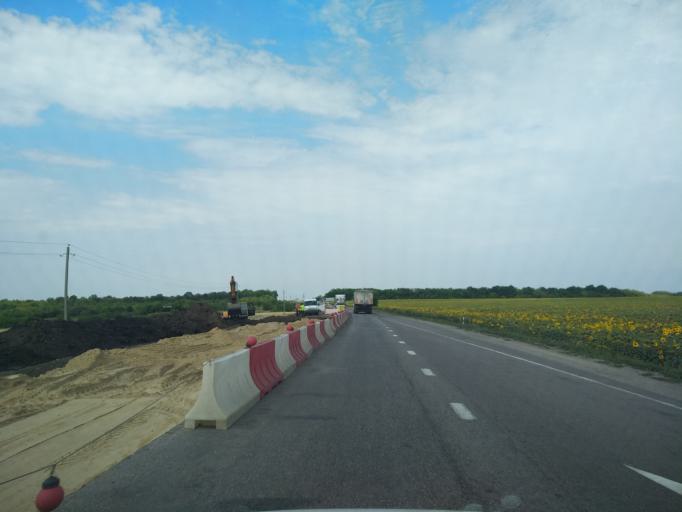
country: RU
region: Voronezj
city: Verkhnyaya Khava
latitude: 51.6779
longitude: 39.8000
